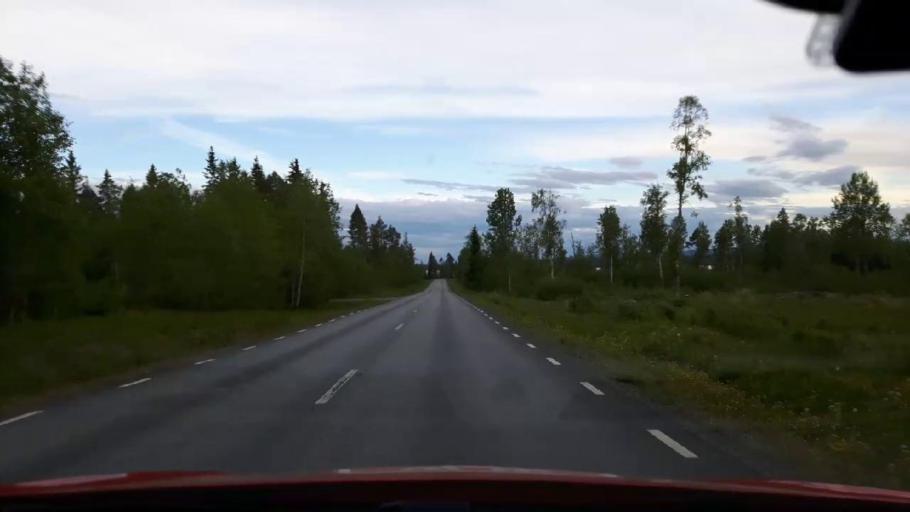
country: SE
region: Jaemtland
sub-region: Bergs Kommun
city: Hoverberg
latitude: 63.0026
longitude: 14.4863
